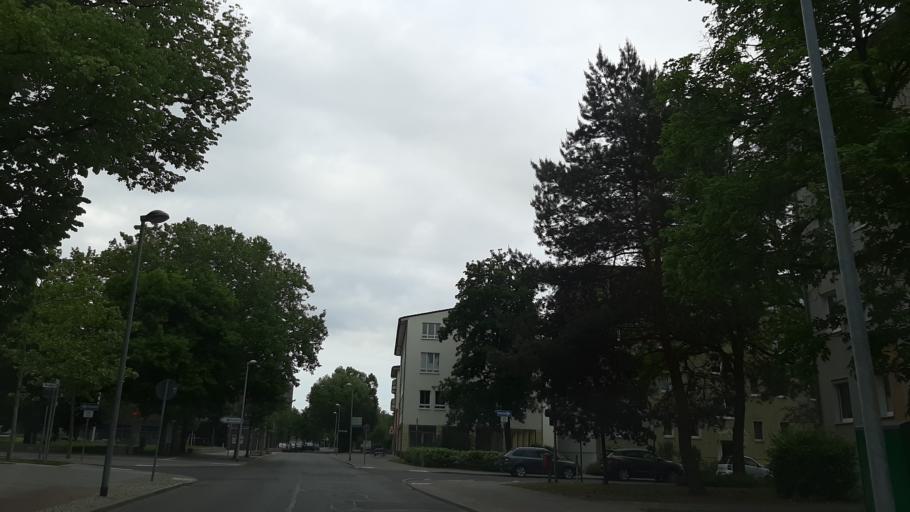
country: DE
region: Brandenburg
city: Hennigsdorf
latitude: 52.6380
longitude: 13.2035
